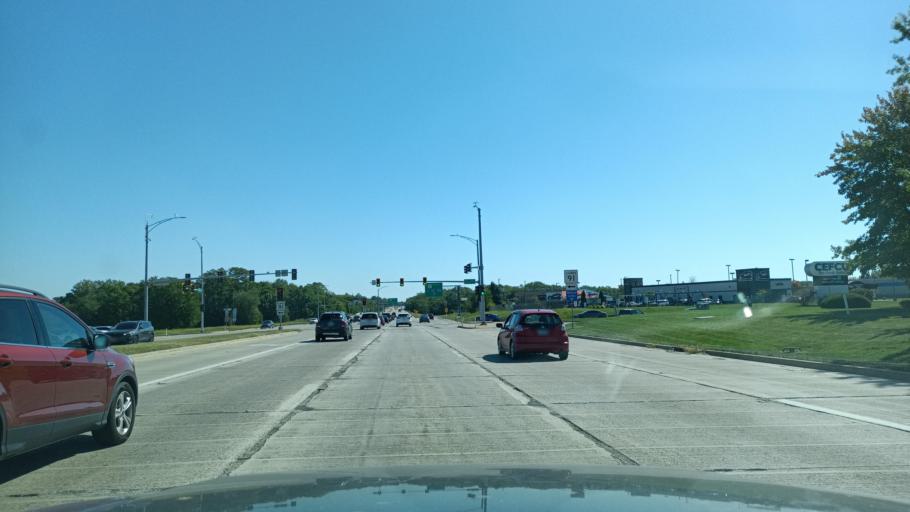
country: US
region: Illinois
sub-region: Peoria County
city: Dunlap
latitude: 40.7765
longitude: -89.6751
